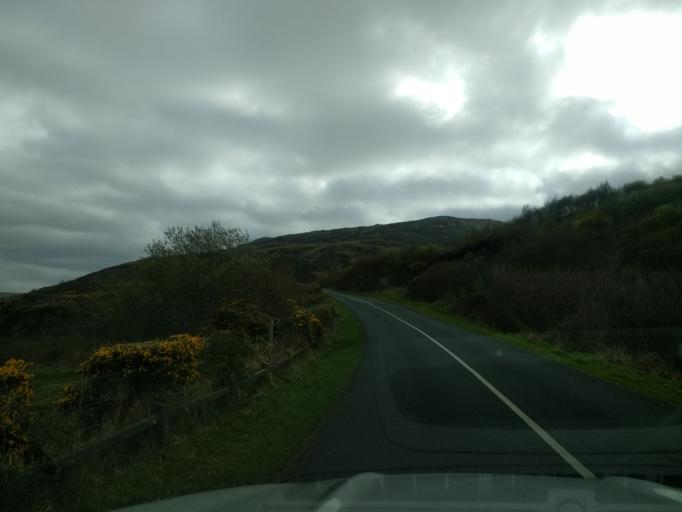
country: IE
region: Ulster
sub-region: County Donegal
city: Ramelton
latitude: 55.1858
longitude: -7.6056
